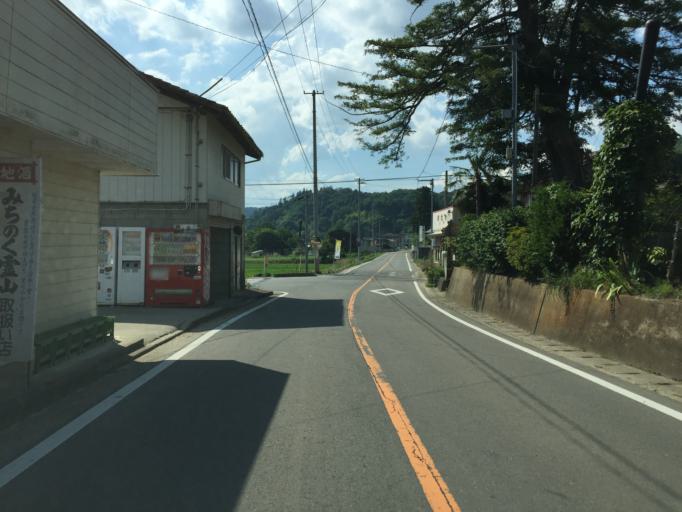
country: JP
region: Fukushima
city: Yanagawamachi-saiwaicho
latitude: 37.8025
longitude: 140.6324
